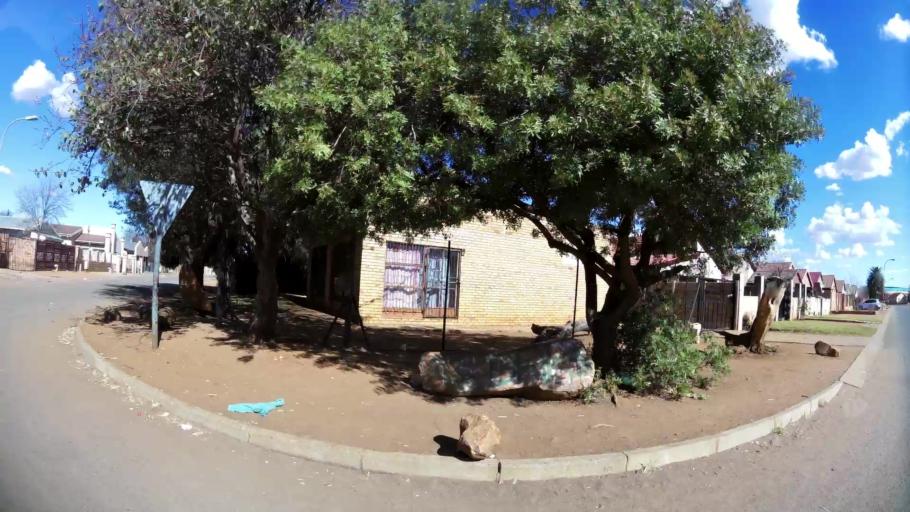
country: ZA
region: North-West
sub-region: Dr Kenneth Kaunda District Municipality
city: Klerksdorp
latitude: -26.8684
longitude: 26.5869
